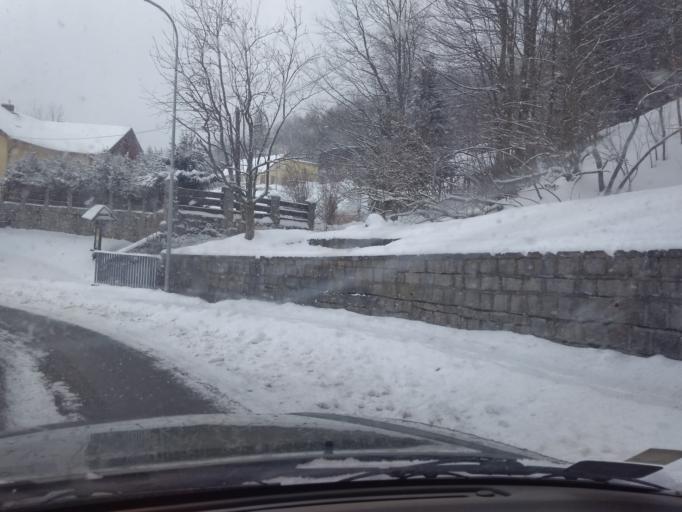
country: PL
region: Lower Silesian Voivodeship
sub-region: Powiat jeleniogorski
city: Karpacz
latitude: 50.7746
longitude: 15.7265
